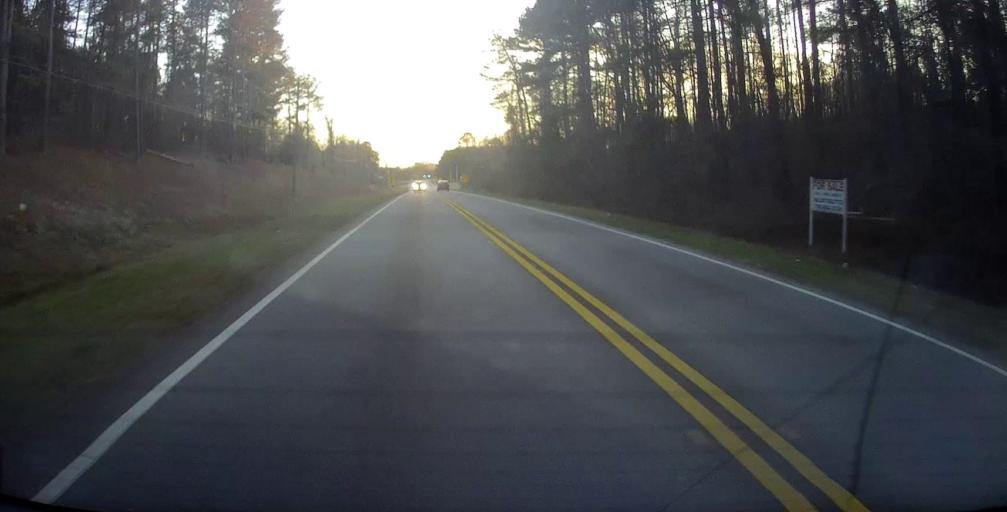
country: US
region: Georgia
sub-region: Troup County
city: La Grange
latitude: 33.0243
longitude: -84.9920
